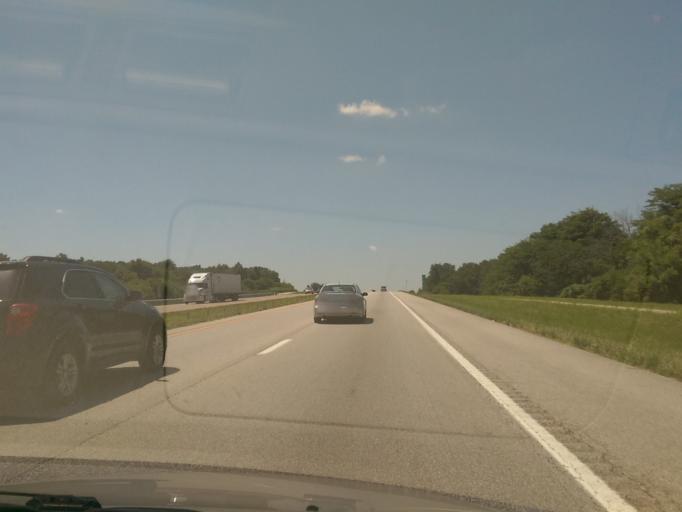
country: US
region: Missouri
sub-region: Cooper County
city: Boonville
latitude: 38.9353
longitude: -92.8813
